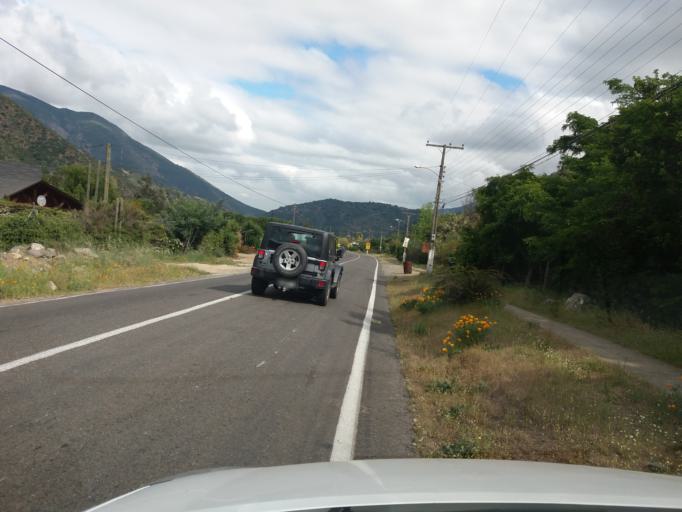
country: CL
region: Valparaiso
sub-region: Provincia de Marga Marga
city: Limache
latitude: -33.0588
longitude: -71.0816
